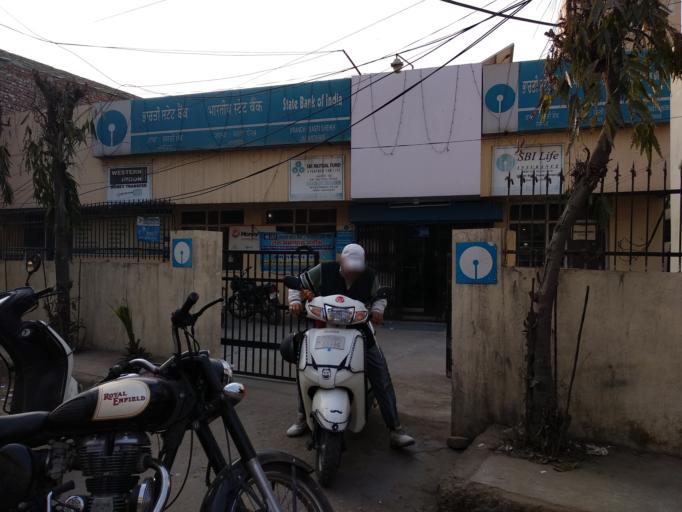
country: IN
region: Punjab
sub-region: Jalandhar
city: Jalandhar
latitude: 31.3211
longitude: 75.5563
